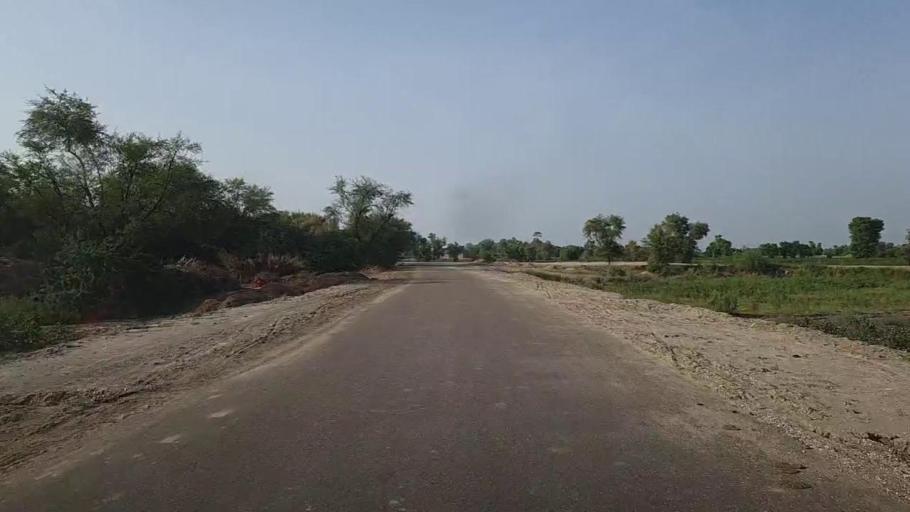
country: PK
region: Sindh
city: Ubauro
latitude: 28.0995
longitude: 69.8455
